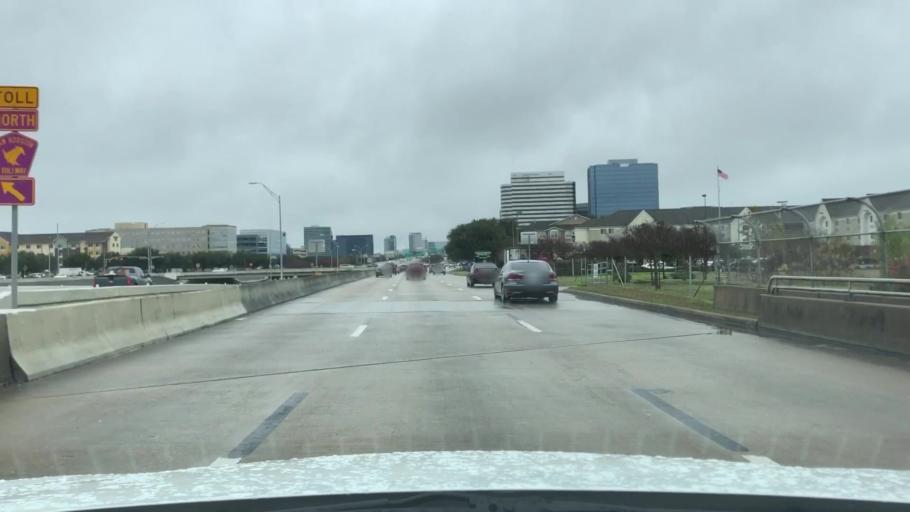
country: US
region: Texas
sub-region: Harris County
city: Bunker Hill Village
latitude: 29.7194
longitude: -95.5566
